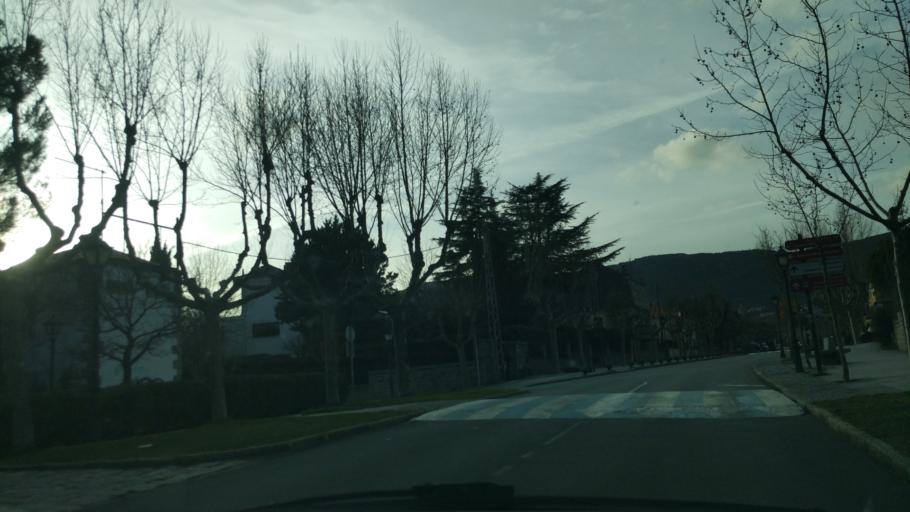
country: ES
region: Madrid
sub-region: Provincia de Madrid
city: El Escorial
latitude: 40.5816
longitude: -4.1274
